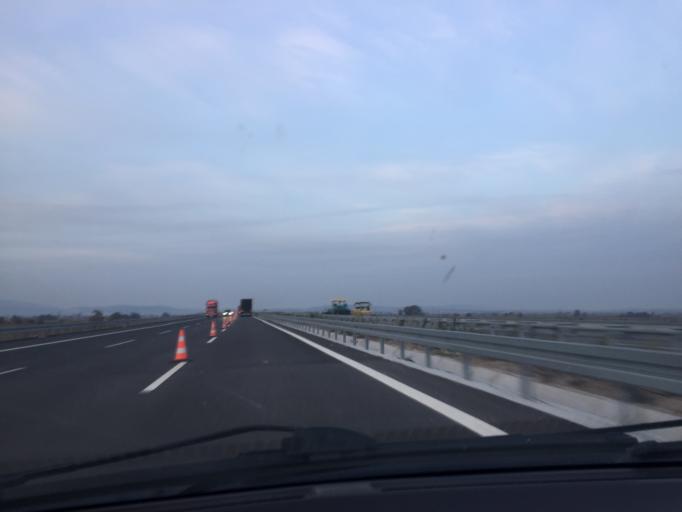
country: TR
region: Manisa
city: Halitpasa
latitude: 38.7247
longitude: 27.6532
